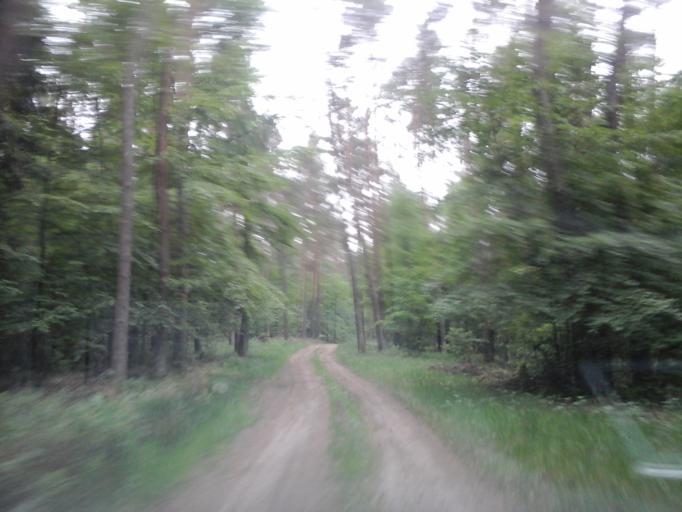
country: PL
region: West Pomeranian Voivodeship
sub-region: Powiat choszczenski
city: Pelczyce
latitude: 52.9505
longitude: 15.3500
